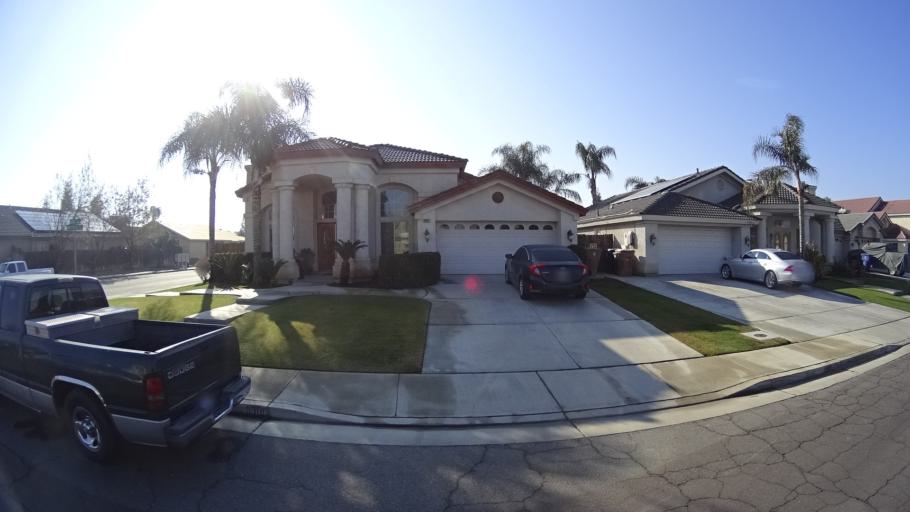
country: US
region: California
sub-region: Kern County
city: Greenacres
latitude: 35.3090
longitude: -119.1118
